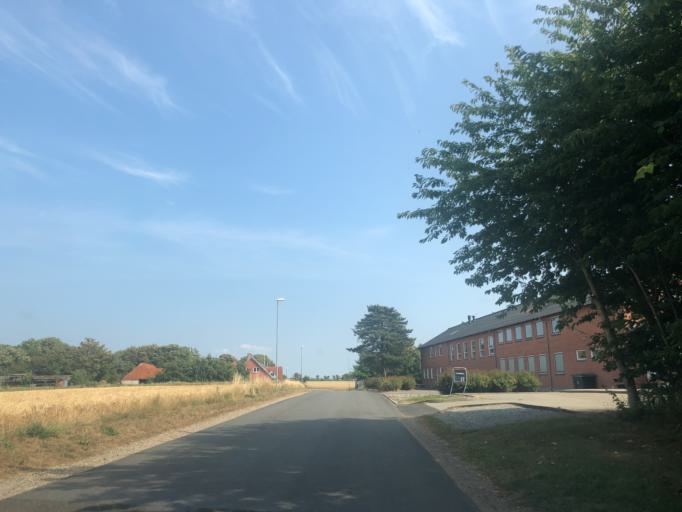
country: DK
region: North Denmark
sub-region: Morso Kommune
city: Nykobing Mors
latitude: 56.8173
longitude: 9.0126
